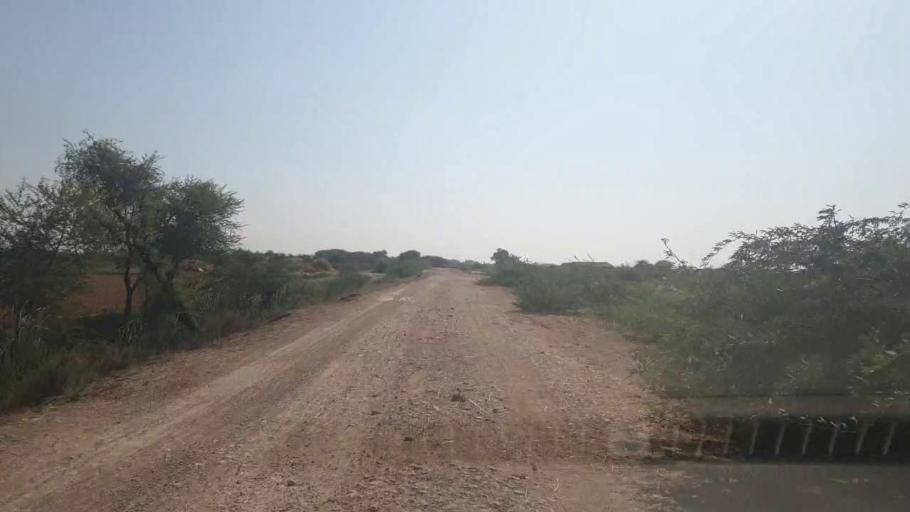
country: PK
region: Sindh
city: Badin
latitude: 24.5584
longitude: 68.8459
